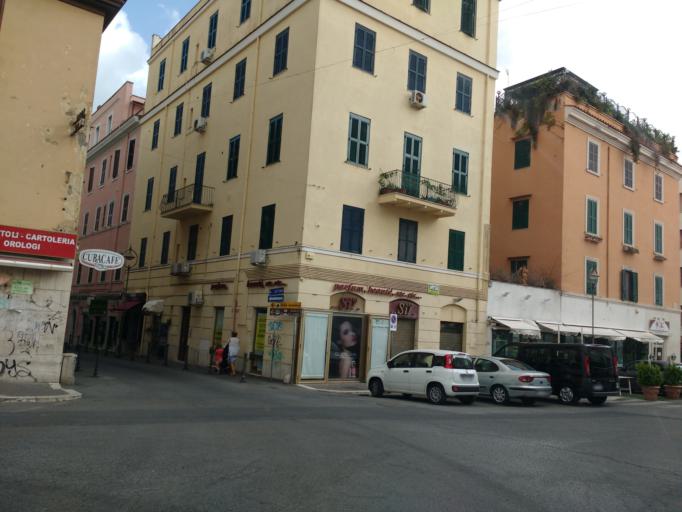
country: IT
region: Latium
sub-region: Citta metropolitana di Roma Capitale
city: Anzio
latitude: 41.4484
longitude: 12.6293
